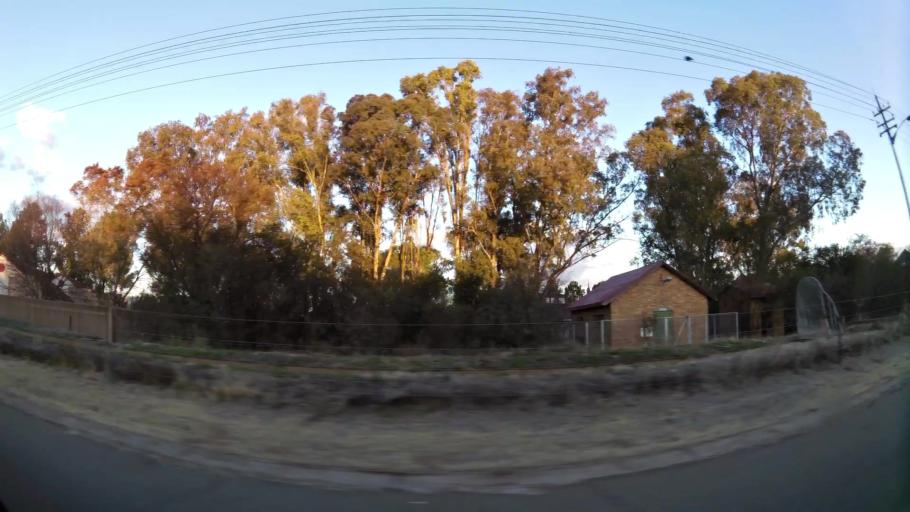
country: ZA
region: North-West
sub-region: Dr Kenneth Kaunda District Municipality
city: Potchefstroom
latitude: -26.6898
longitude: 27.0860
